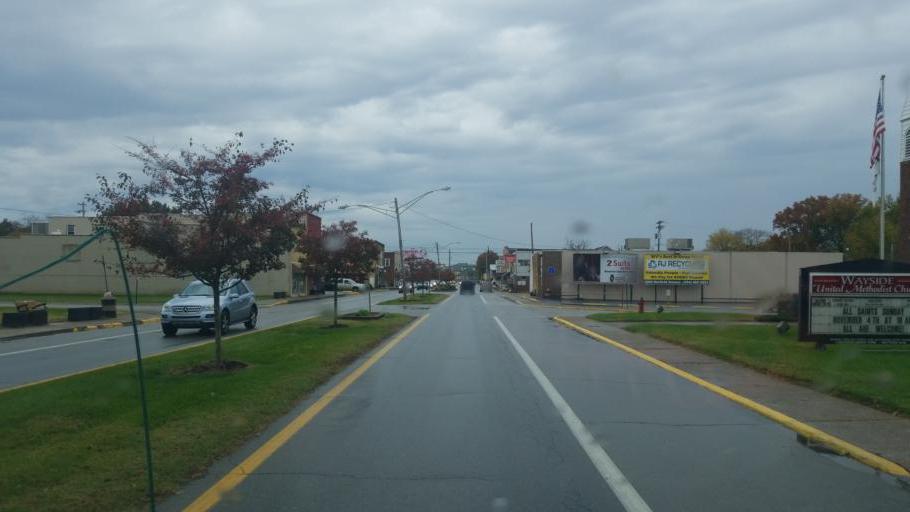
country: US
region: West Virginia
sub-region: Wood County
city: Vienna
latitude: 39.3261
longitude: -81.5493
